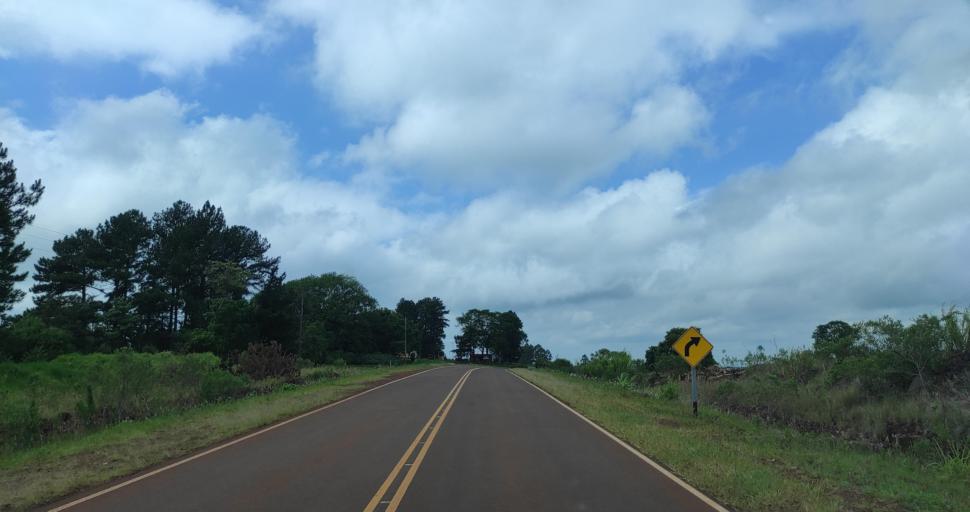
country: AR
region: Misiones
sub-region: Departamento de Veinticinco de Mayo
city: Veinticinco de Mayo
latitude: -27.3585
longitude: -54.8716
